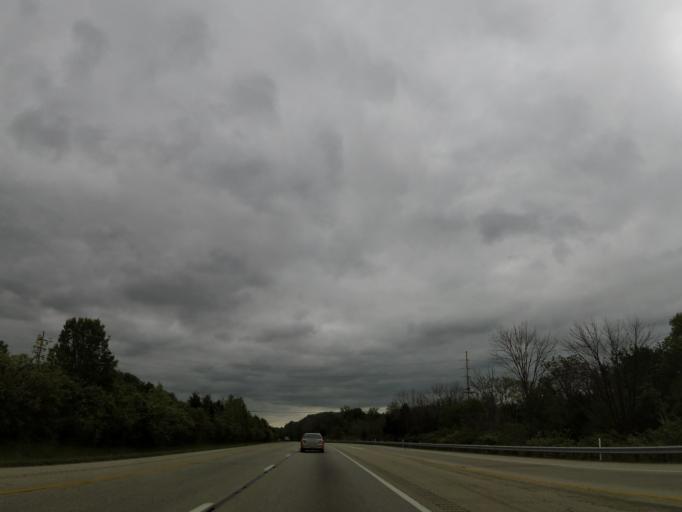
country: US
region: Ohio
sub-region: Warren County
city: South Lebanon
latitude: 39.3845
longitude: -84.2155
